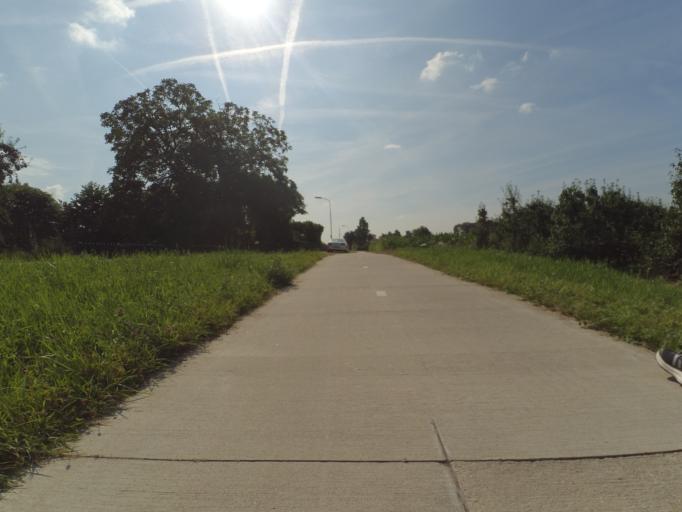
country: NL
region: Utrecht
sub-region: Gemeente Houten
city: Houten
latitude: 52.0121
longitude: 5.2010
